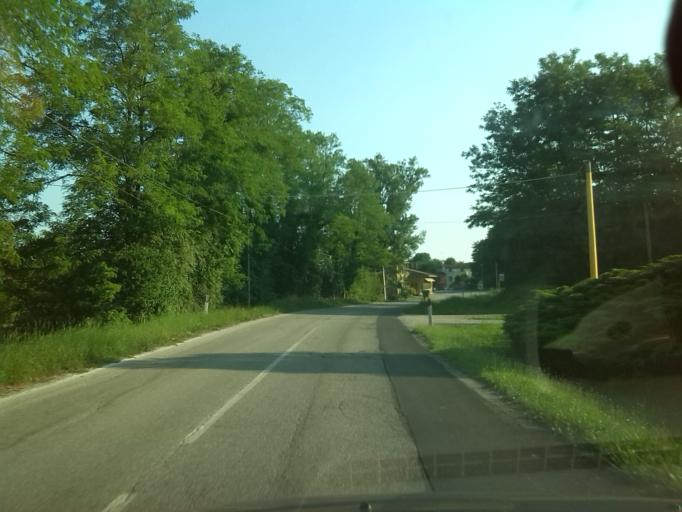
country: IT
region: Friuli Venezia Giulia
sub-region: Provincia di Gorizia
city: Dolegna del Collio
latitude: 46.0337
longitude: 13.4766
